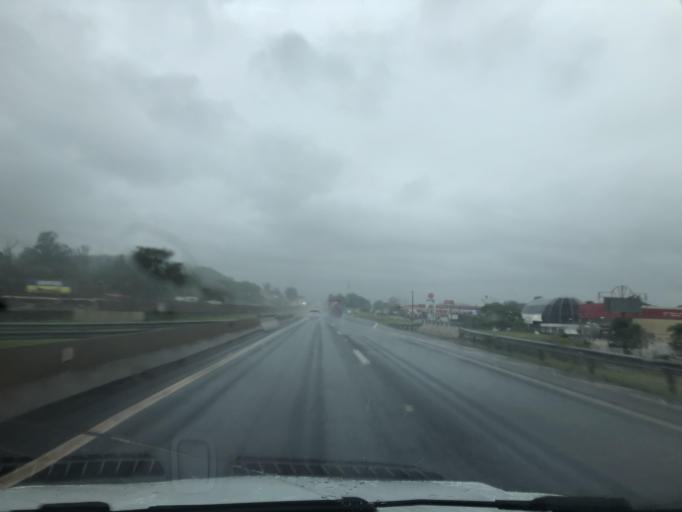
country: BR
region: Sao Paulo
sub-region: Ribeirao Preto
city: Ribeirao Preto
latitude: -21.2229
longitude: -47.7593
